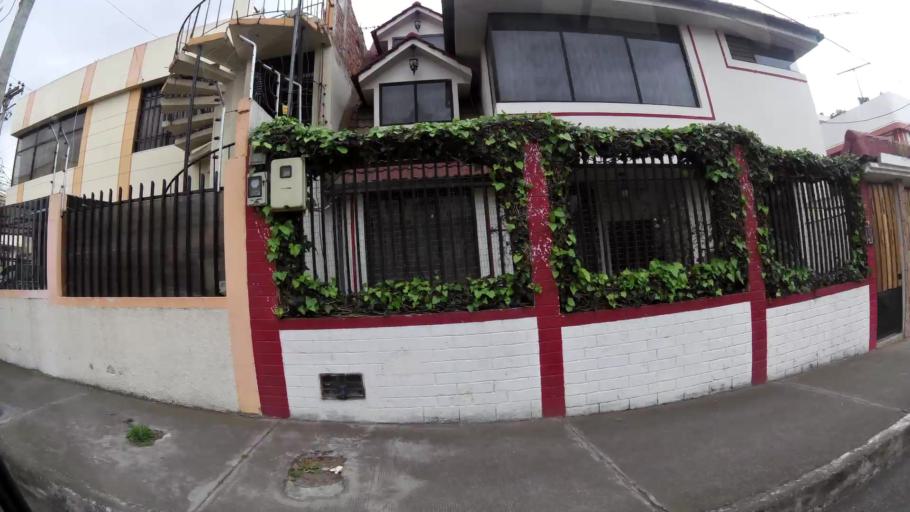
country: EC
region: Tungurahua
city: Ambato
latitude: -1.2604
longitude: -78.6280
